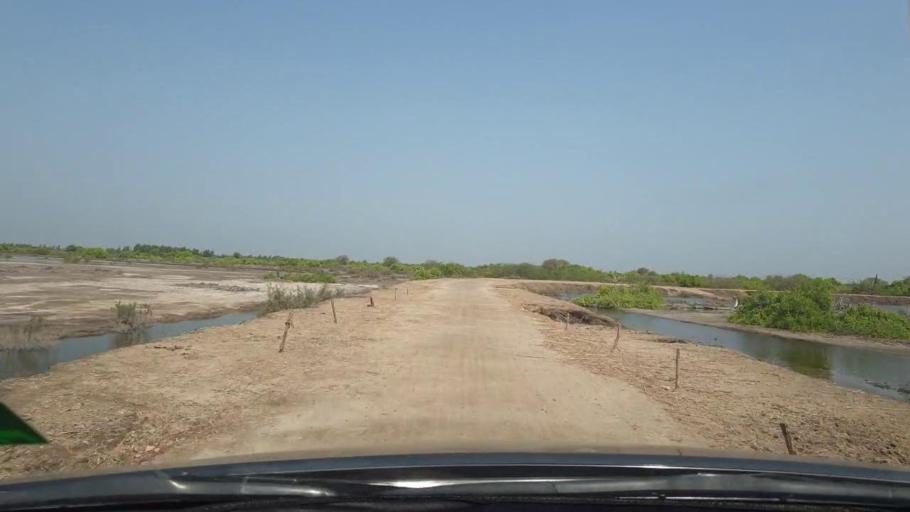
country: PK
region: Sindh
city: Tando Bago
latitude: 24.8042
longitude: 69.1083
